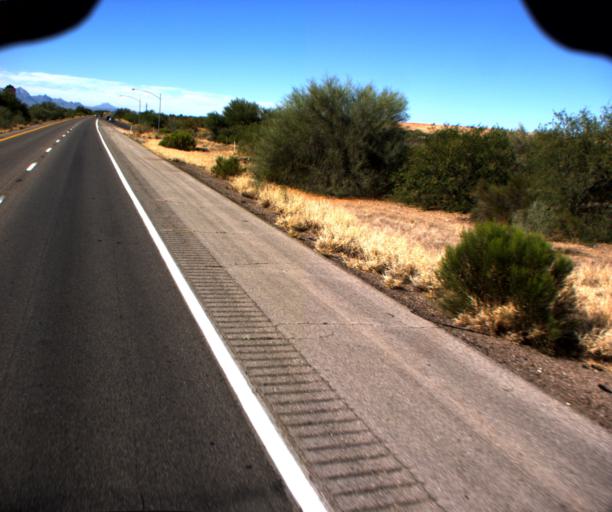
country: US
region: Arizona
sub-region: Pima County
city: Sahuarita
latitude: 31.9556
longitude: -110.9876
